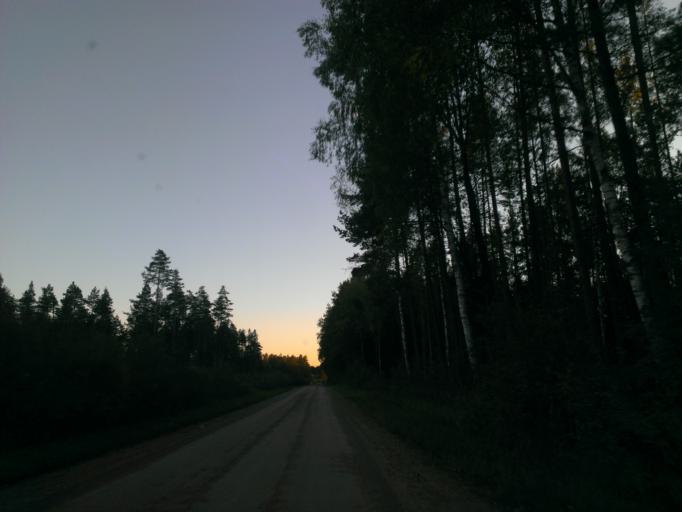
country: LV
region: Incukalns
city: Vangazi
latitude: 57.1105
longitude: 24.5654
